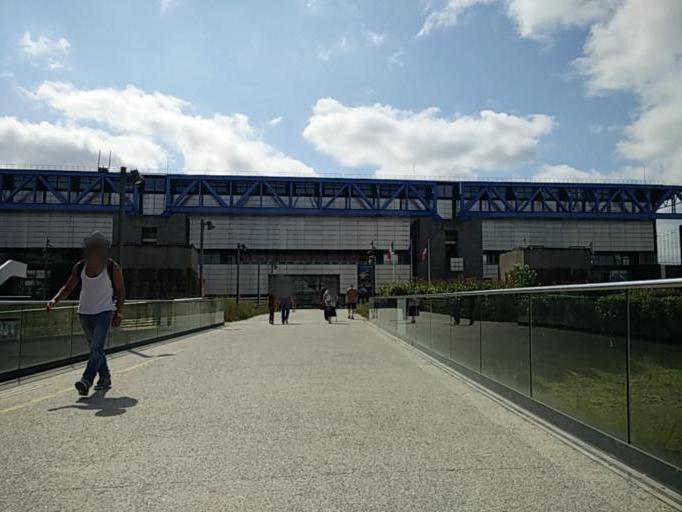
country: FR
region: Ile-de-France
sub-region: Departement de Seine-Saint-Denis
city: Aubervilliers
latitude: 48.8968
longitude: 2.3863
